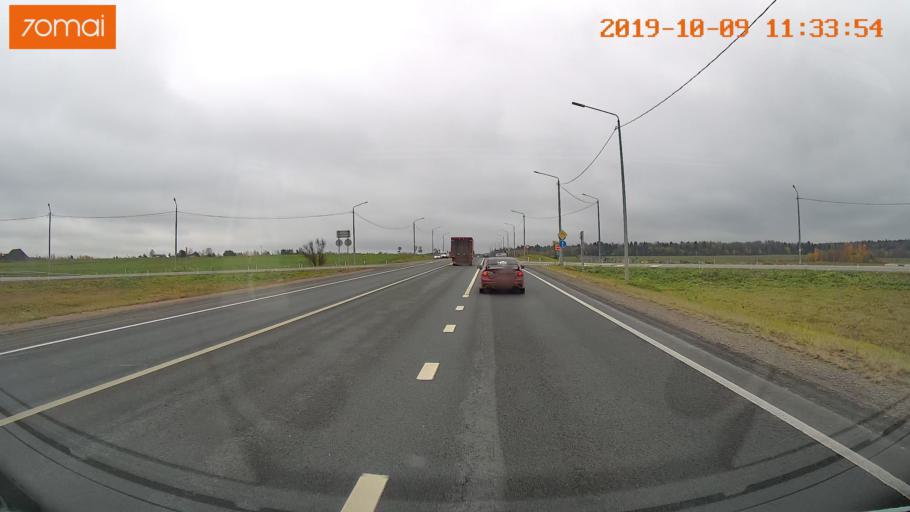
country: RU
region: Vologda
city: Gryazovets
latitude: 59.0209
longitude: 40.1158
